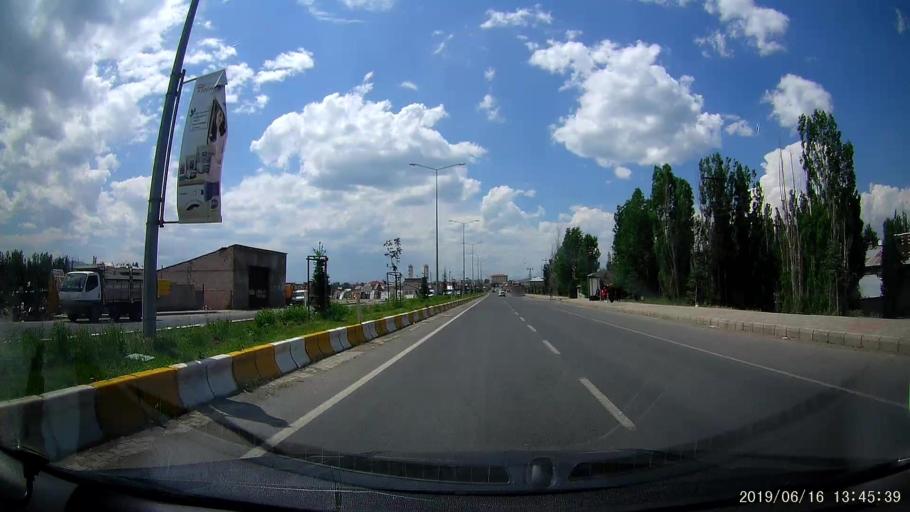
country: TR
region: Agri
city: Agri
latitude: 39.7097
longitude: 43.0427
